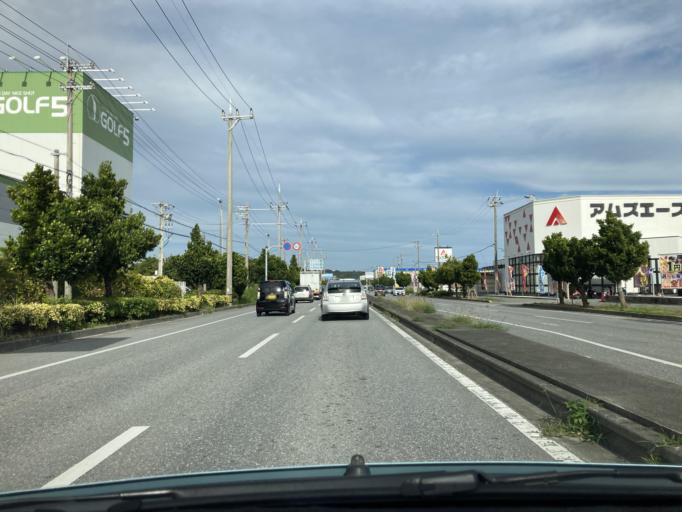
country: JP
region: Okinawa
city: Katsuren-haebaru
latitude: 26.3365
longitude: 127.8448
